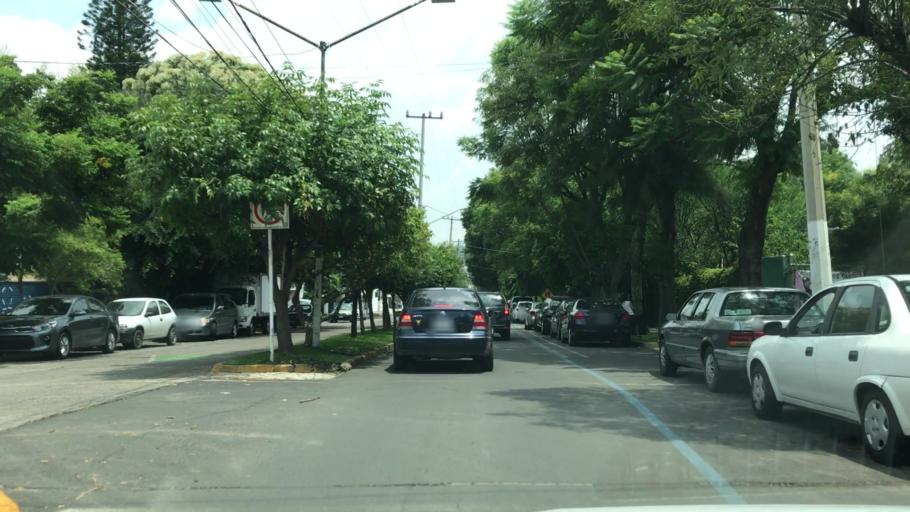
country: MX
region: Jalisco
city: Guadalajara
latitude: 20.6604
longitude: -103.4066
